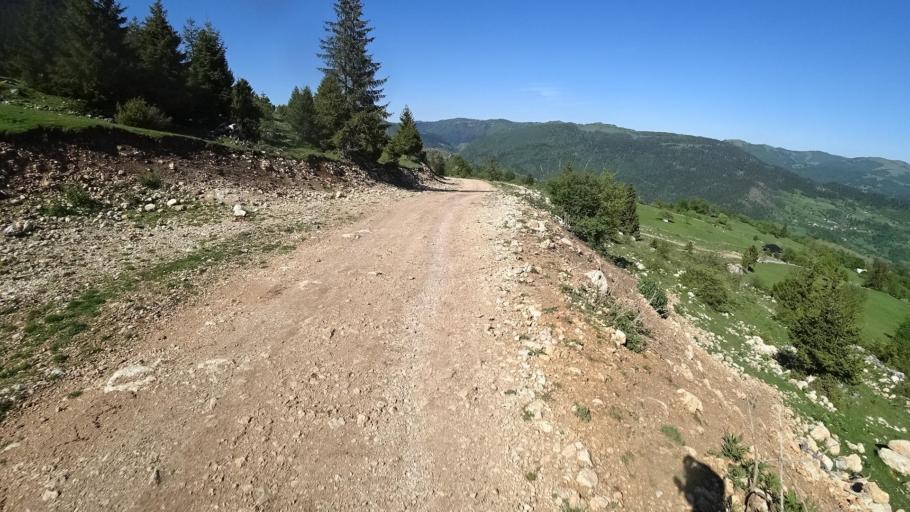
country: BA
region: Federation of Bosnia and Herzegovina
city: Travnik
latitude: 44.2865
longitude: 17.6958
